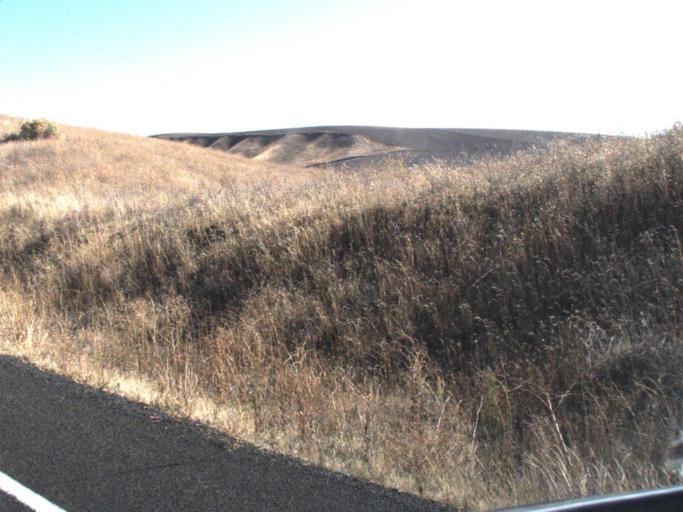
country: US
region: Washington
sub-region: Walla Walla County
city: Garrett
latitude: 46.2889
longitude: -118.4855
